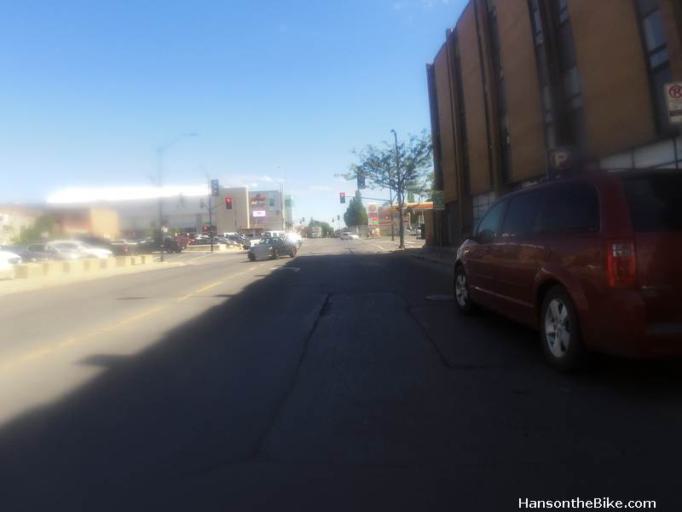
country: CA
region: Ontario
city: Kingston
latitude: 44.2316
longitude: -76.4793
